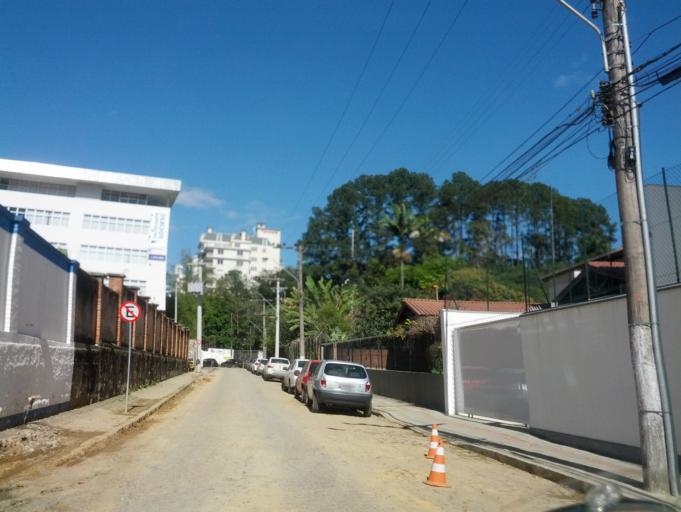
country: BR
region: Santa Catarina
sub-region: Blumenau
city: Blumenau
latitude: -26.9257
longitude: -49.0646
